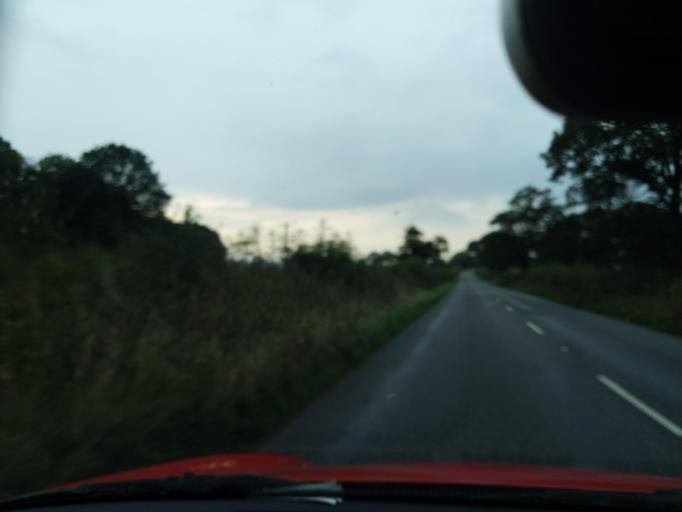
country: GB
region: England
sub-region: Devon
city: Okehampton
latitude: 50.7983
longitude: -4.0488
